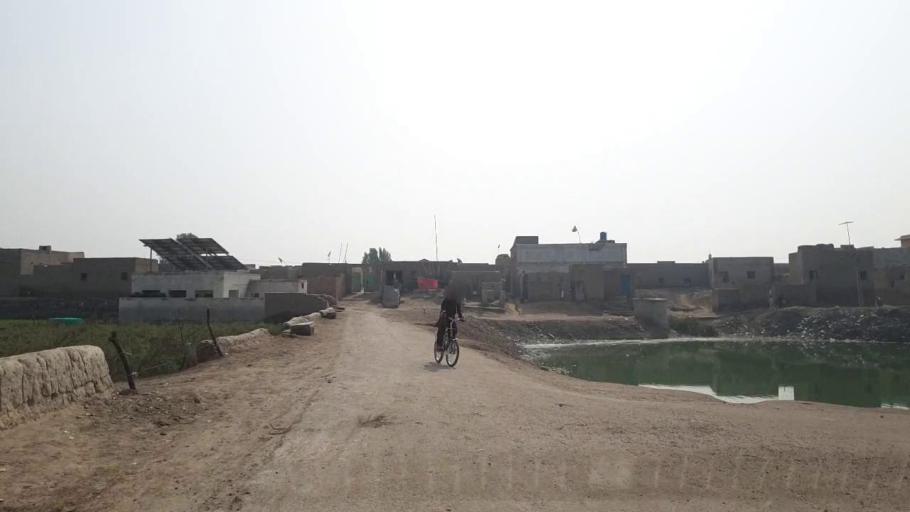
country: PK
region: Sindh
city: Bhan
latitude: 26.4466
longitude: 67.7154
